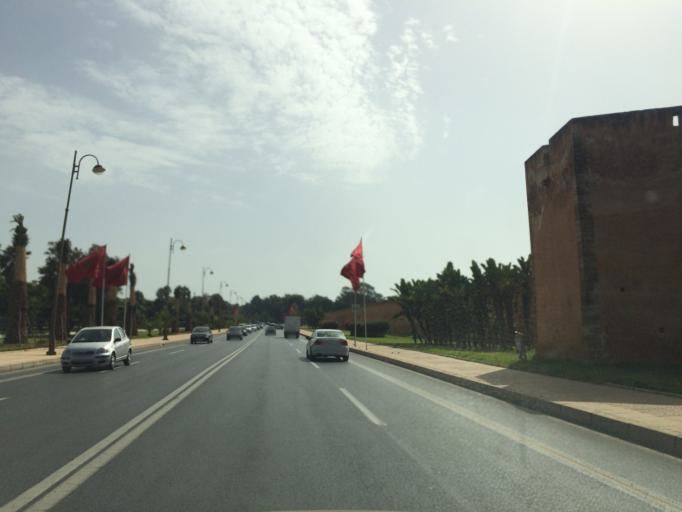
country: MA
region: Rabat-Sale-Zemmour-Zaer
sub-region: Rabat
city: Rabat
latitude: 34.0013
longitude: -6.8328
